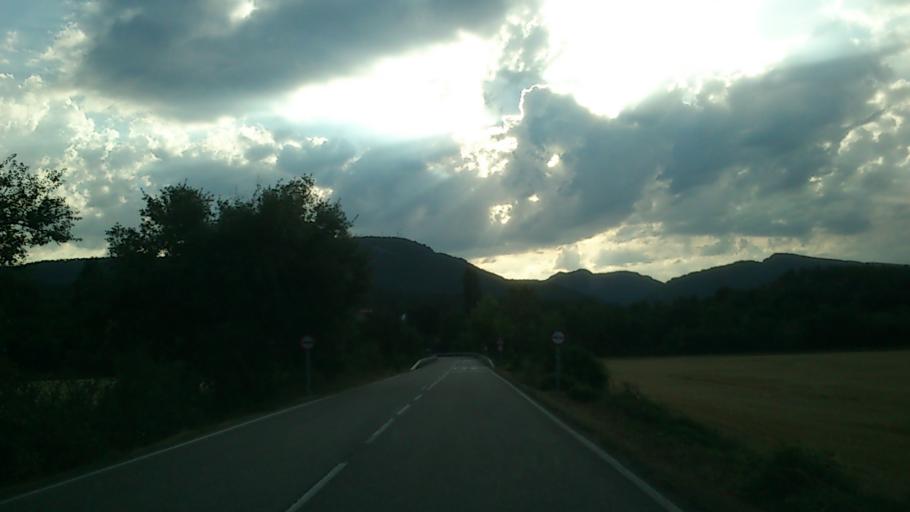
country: ES
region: Castille and Leon
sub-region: Provincia de Burgos
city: Trespaderne
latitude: 42.7886
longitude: -3.3589
